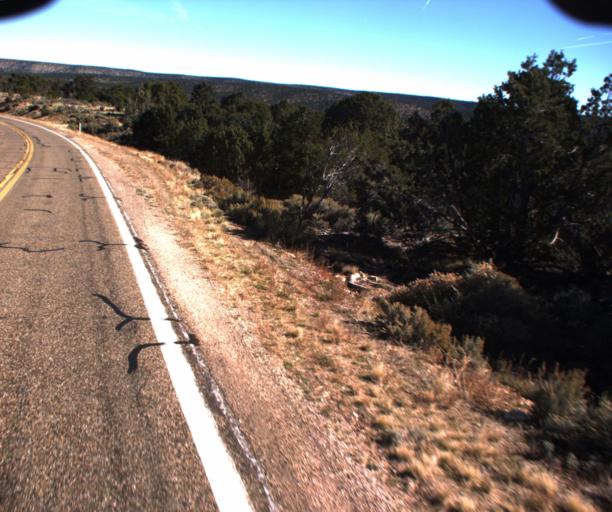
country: US
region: Arizona
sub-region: Coconino County
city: Fredonia
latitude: 36.8403
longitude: -112.2549
